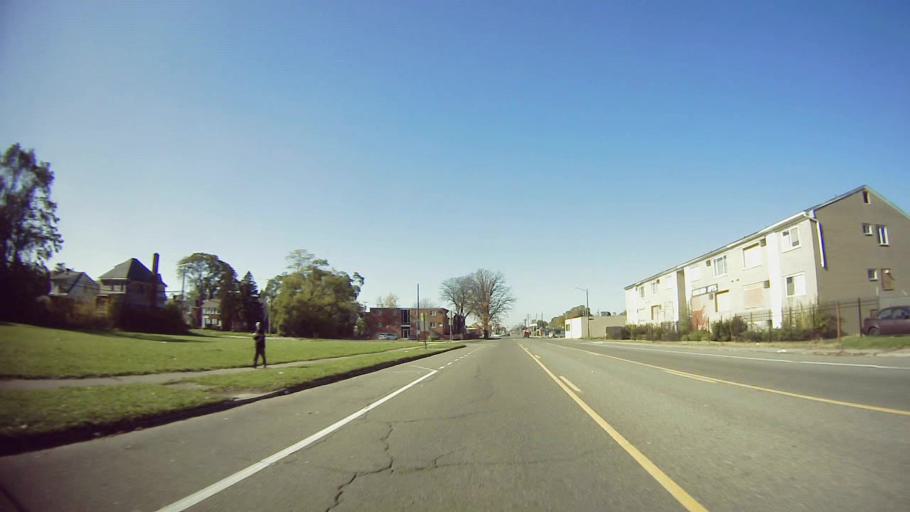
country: US
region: Michigan
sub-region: Wayne County
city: Dearborn
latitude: 42.3658
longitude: -83.1744
